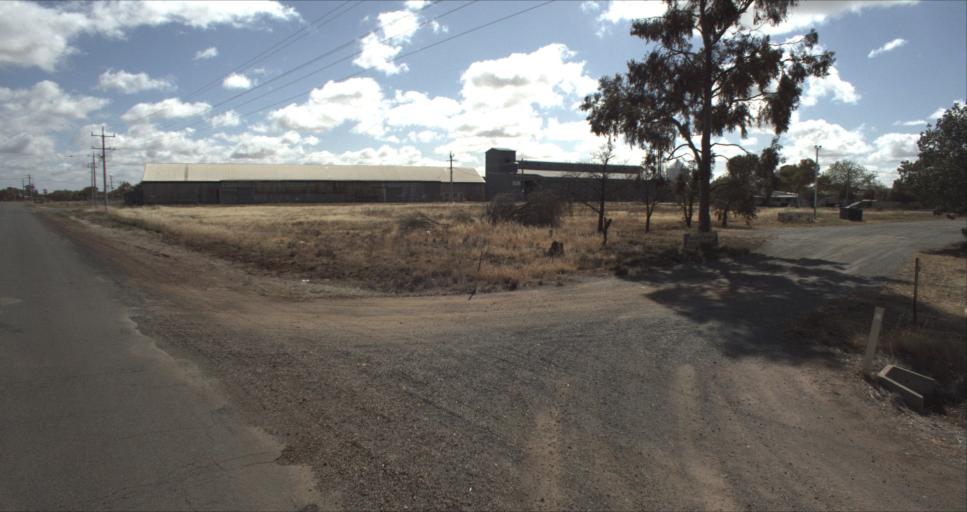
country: AU
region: New South Wales
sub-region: Murrumbidgee Shire
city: Darlington Point
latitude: -34.5158
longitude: 146.1766
